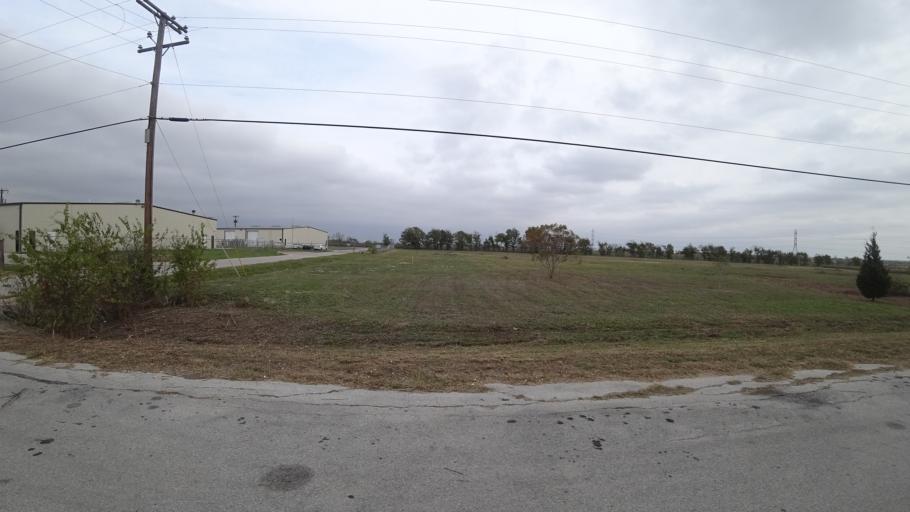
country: US
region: Texas
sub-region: Travis County
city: Manor
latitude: 30.3902
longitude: -97.5832
